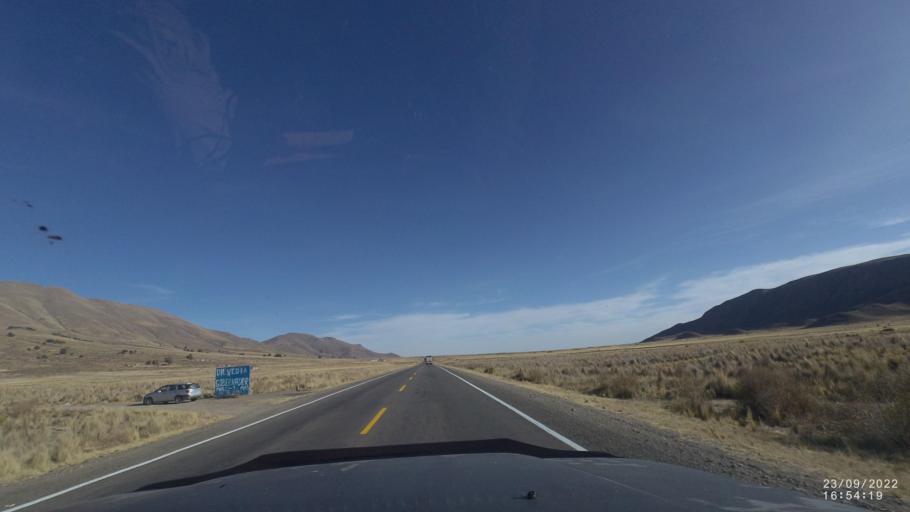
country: BO
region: Oruro
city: Poopo
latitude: -18.4618
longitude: -66.9697
